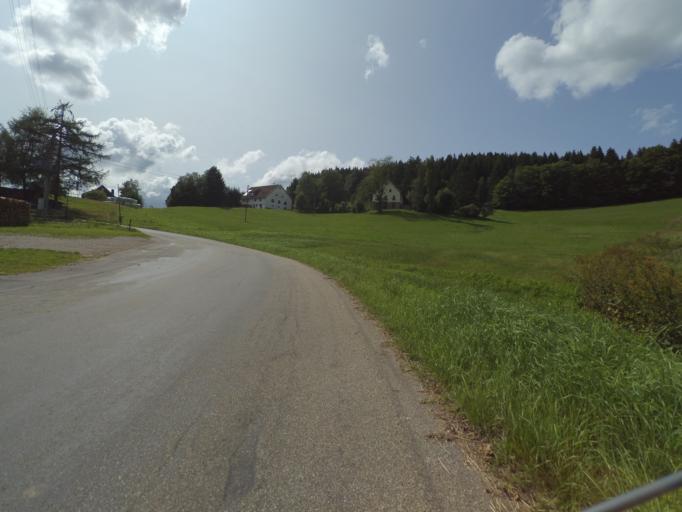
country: DE
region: Baden-Wuerttemberg
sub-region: Freiburg Region
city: Friedenweiler
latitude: 47.9184
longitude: 8.2357
